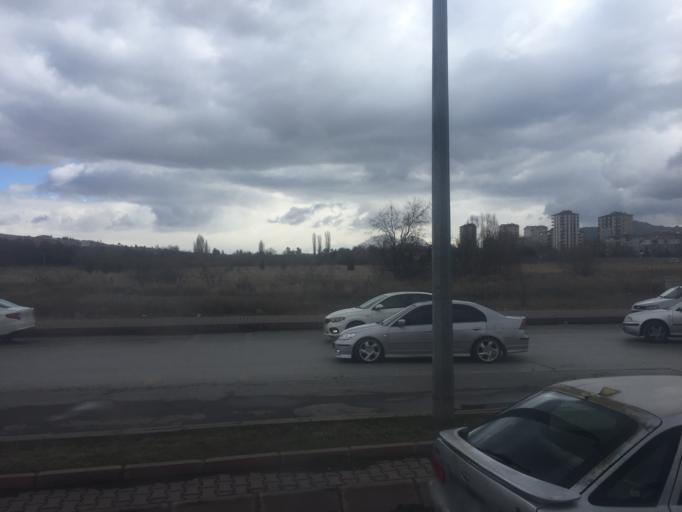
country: TR
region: Kayseri
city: Melikgazi
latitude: 38.7496
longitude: 35.4048
